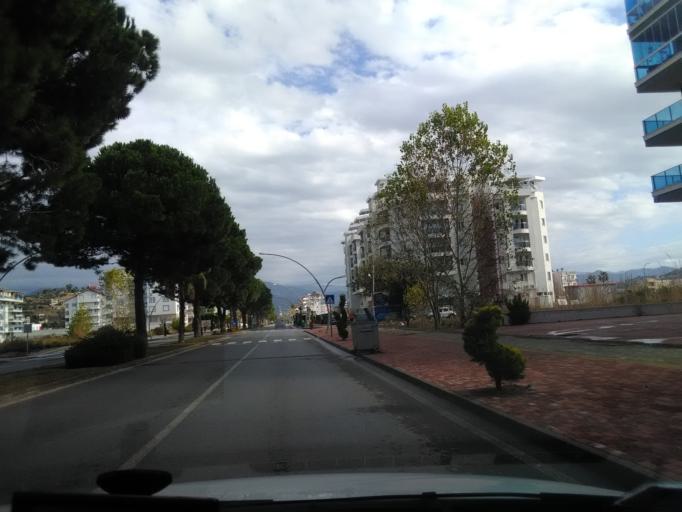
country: TR
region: Antalya
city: Gazipasa
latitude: 36.2654
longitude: 32.2934
